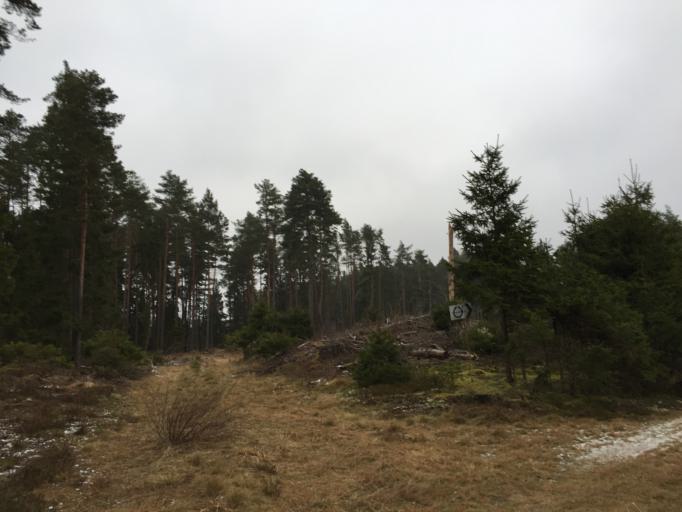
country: EE
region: Saare
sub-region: Kuressaare linn
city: Kuressaare
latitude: 58.4991
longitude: 22.3779
